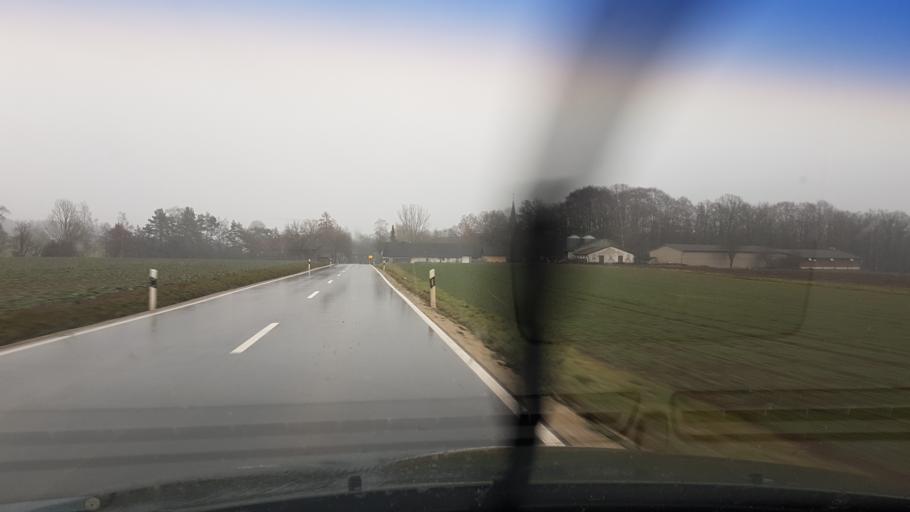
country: DE
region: Bavaria
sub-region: Upper Franconia
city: Wonsees
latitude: 50.0278
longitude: 11.2967
